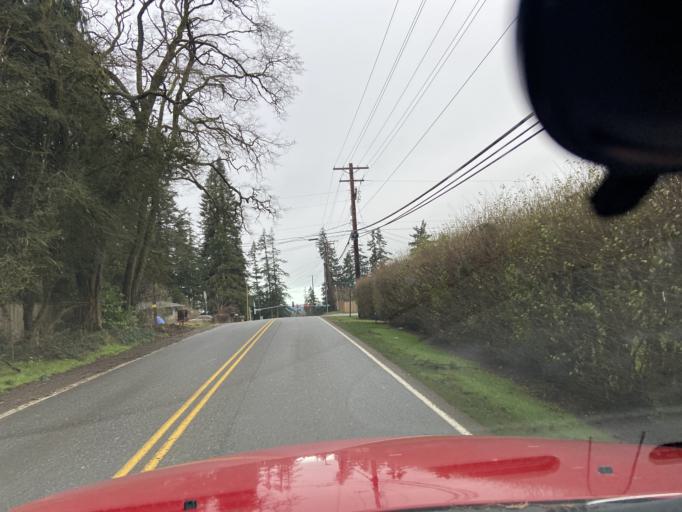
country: US
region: Washington
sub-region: Snohomish County
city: West Lake Stevens
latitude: 47.9673
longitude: -122.1000
